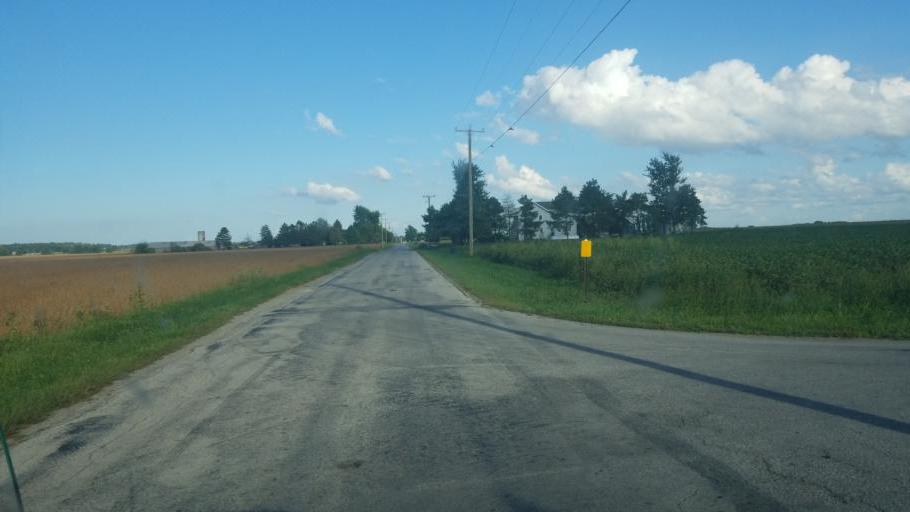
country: US
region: Ohio
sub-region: Hancock County
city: Arlington
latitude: 40.9356
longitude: -83.6136
